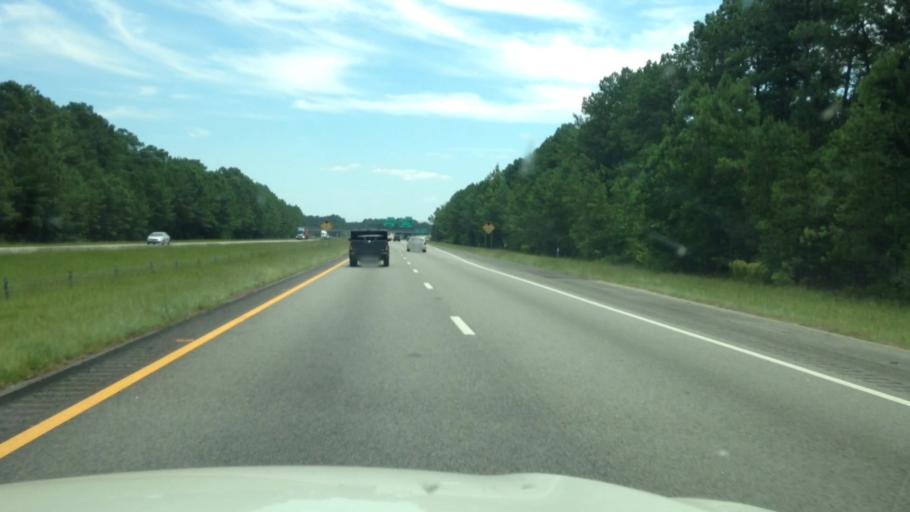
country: US
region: South Carolina
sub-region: Florence County
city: Florence
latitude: 34.1991
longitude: -79.8575
